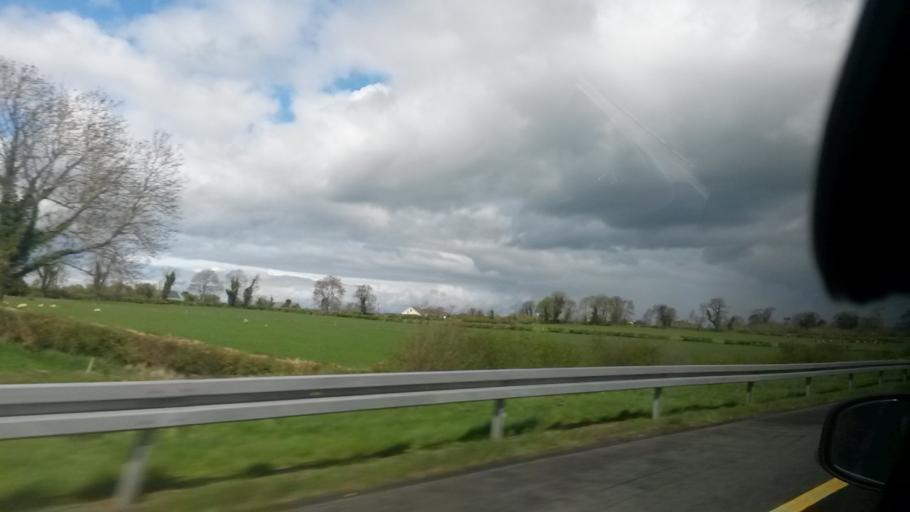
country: IE
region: Munster
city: Cahir
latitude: 52.4464
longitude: -7.9098
